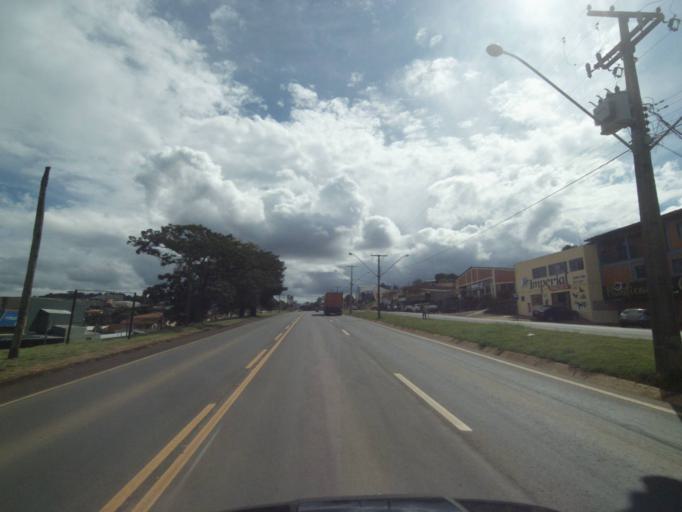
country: BR
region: Parana
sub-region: Telemaco Borba
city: Telemaco Borba
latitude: -24.3291
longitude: -50.6364
